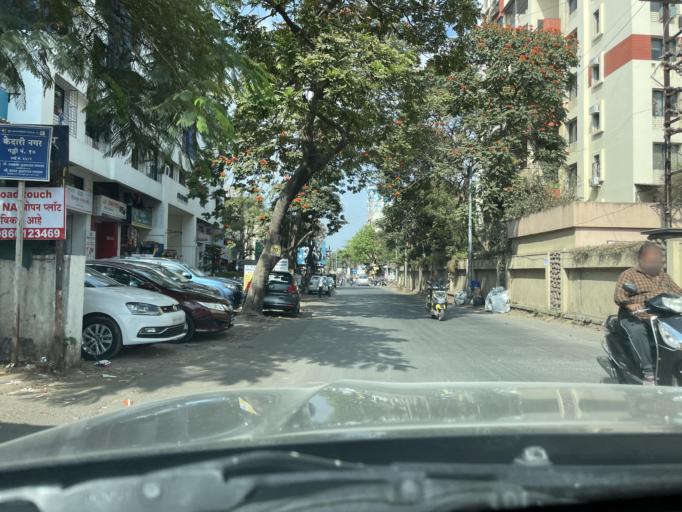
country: IN
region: Maharashtra
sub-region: Pune Division
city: Pune
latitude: 18.4834
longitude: 73.9006
